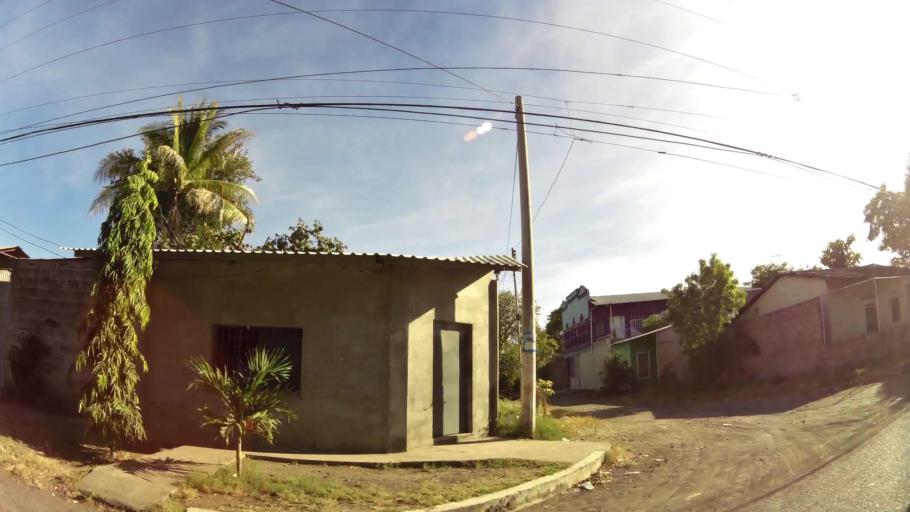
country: SV
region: San Miguel
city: San Miguel
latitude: 13.4682
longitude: -88.1931
